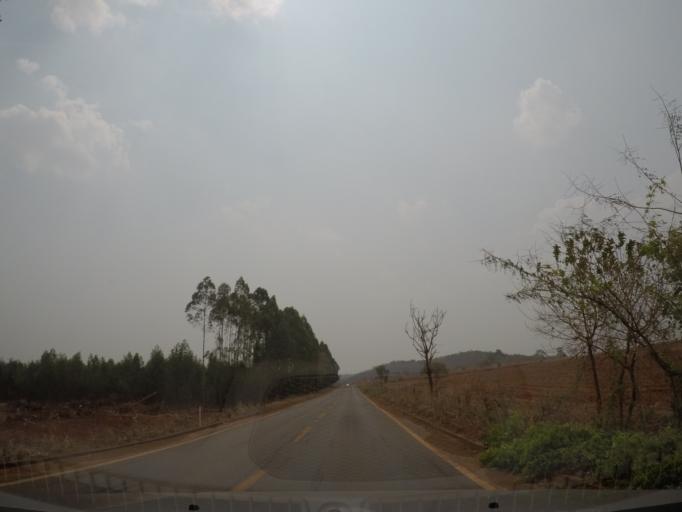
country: BR
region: Goias
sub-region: Pirenopolis
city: Pirenopolis
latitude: -15.9069
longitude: -48.8632
